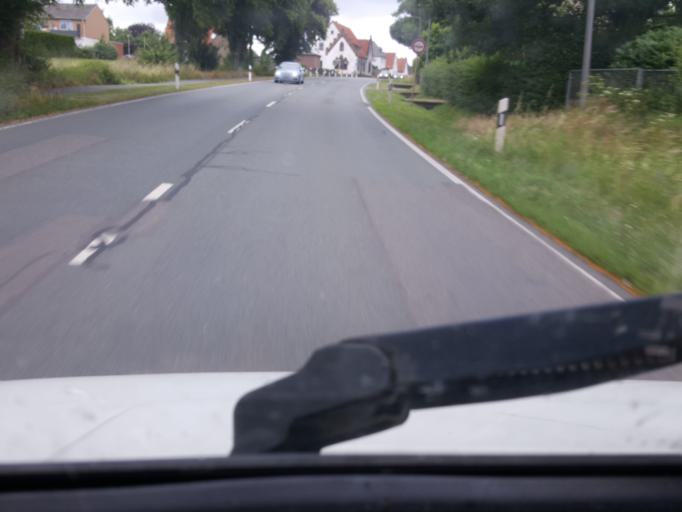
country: DE
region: North Rhine-Westphalia
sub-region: Regierungsbezirk Detmold
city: Minden
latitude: 52.3178
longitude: 8.9175
